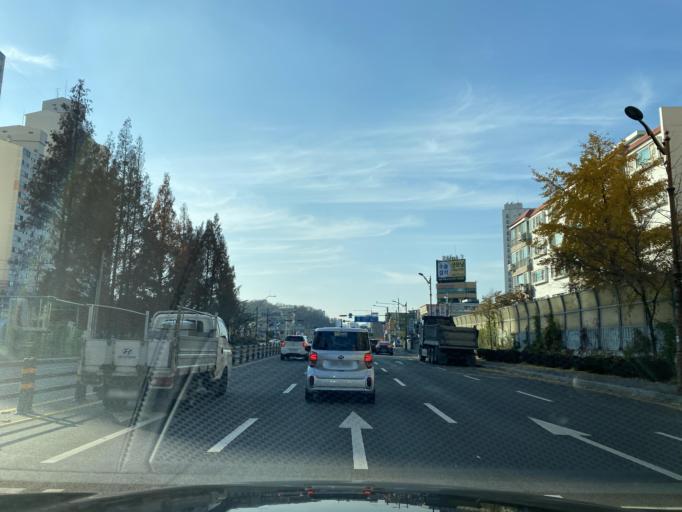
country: KR
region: Chungcheongnam-do
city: Cheonan
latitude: 36.7986
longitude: 127.1555
